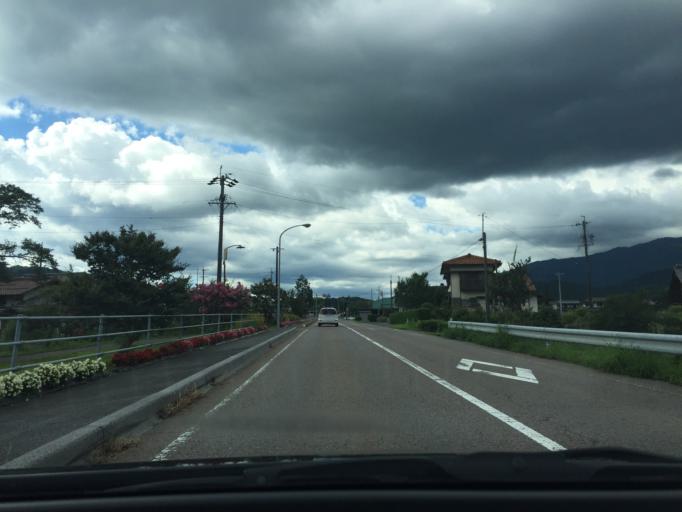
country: JP
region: Gifu
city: Nakatsugawa
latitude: 35.7410
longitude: 137.3412
